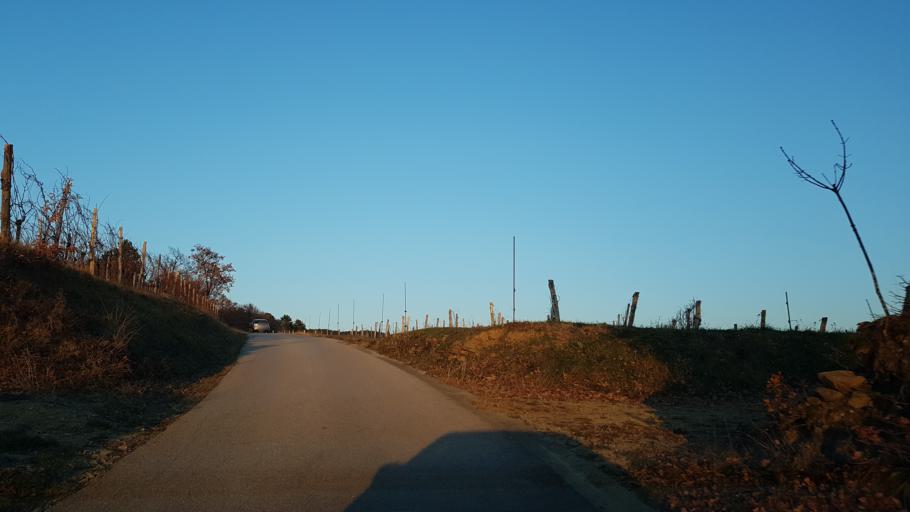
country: SI
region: Koper-Capodistria
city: Sv. Anton
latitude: 45.4944
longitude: 13.8463
